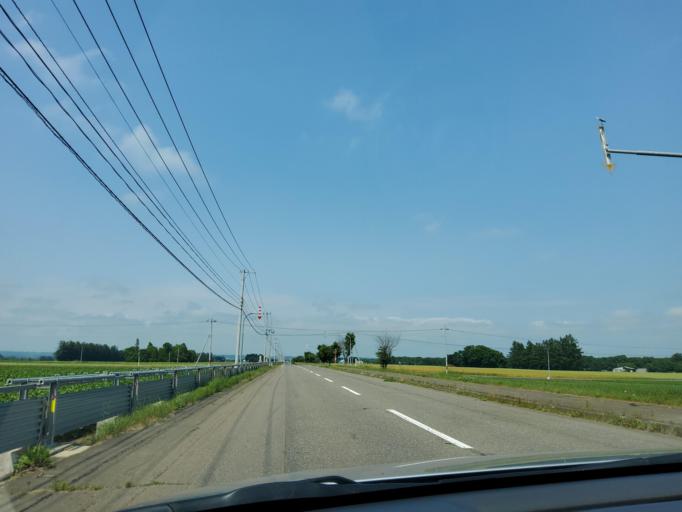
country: JP
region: Hokkaido
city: Obihiro
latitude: 42.8804
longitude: 143.0315
